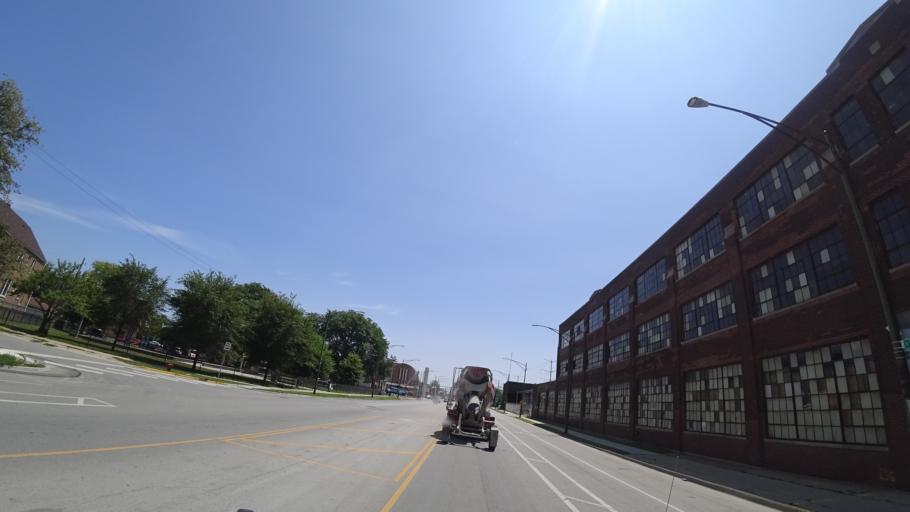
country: US
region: Indiana
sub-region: Lake County
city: Whiting
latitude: 41.7456
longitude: -87.5775
